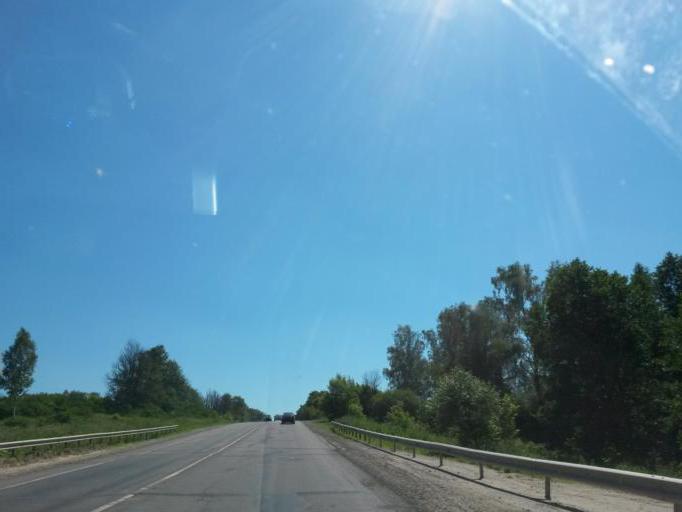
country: RU
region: Moskovskaya
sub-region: Chekhovskiy Rayon
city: Chekhov
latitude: 55.0978
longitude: 37.4439
